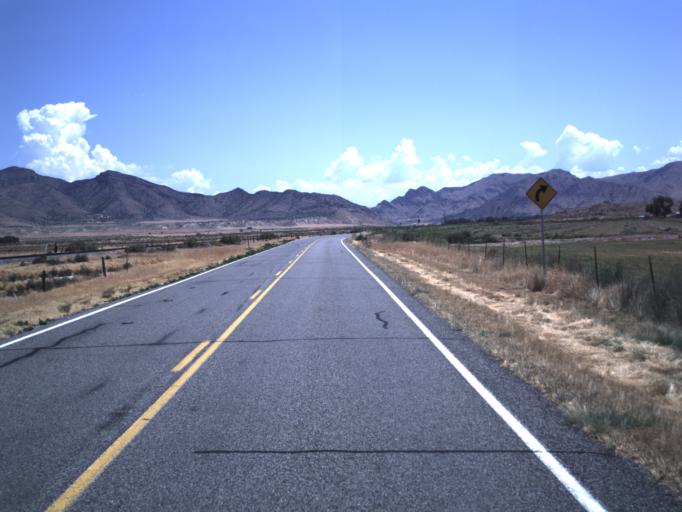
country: US
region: Utah
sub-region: Millard County
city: Delta
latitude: 39.5325
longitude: -112.3312
